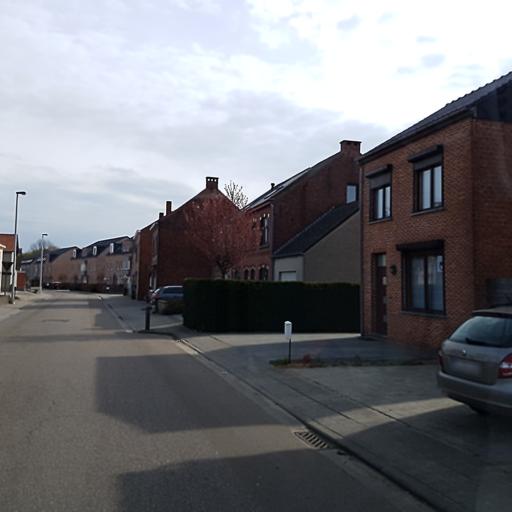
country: BE
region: Flanders
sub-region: Provincie Vlaams-Brabant
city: Aarschot
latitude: 51.0025
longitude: 4.8290
